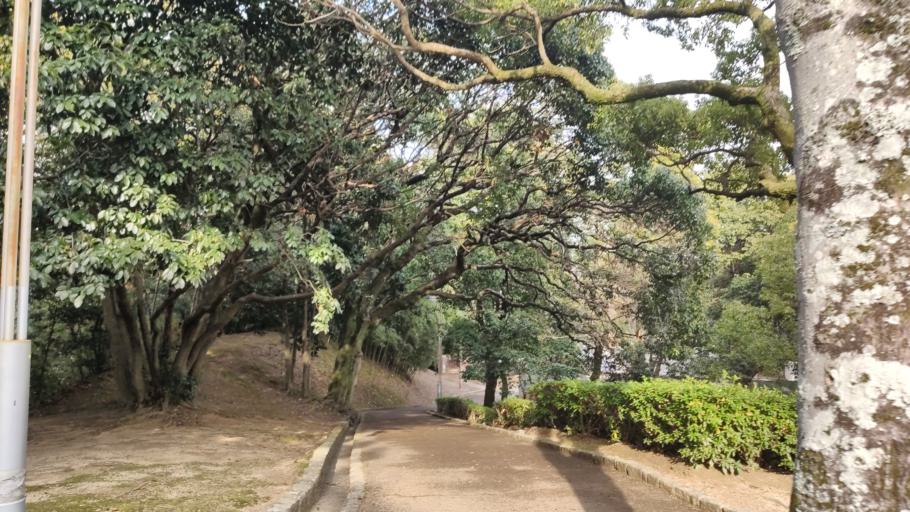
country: JP
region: Hyogo
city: Himeji
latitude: 34.8421
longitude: 134.6927
